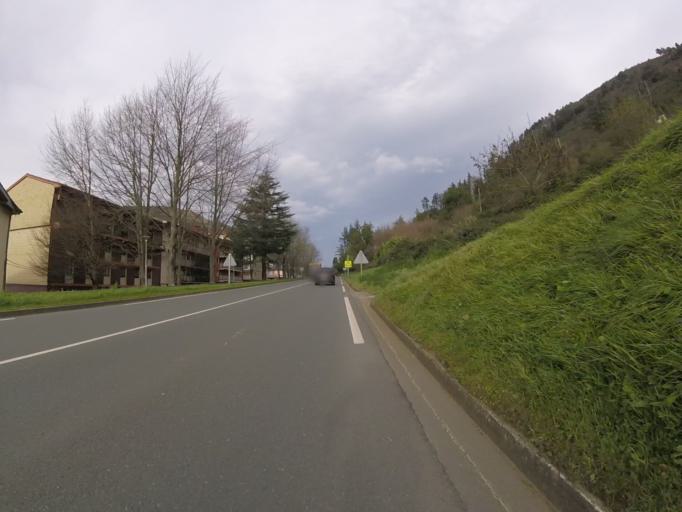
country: ES
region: Basque Country
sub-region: Provincia de Guipuzcoa
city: Cestona
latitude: 43.2388
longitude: -2.2554
